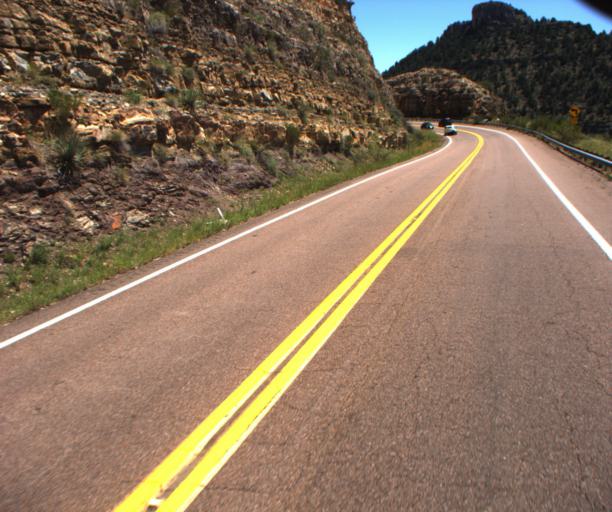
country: US
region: Arizona
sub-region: Navajo County
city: Cibecue
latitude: 33.8086
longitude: -110.4678
